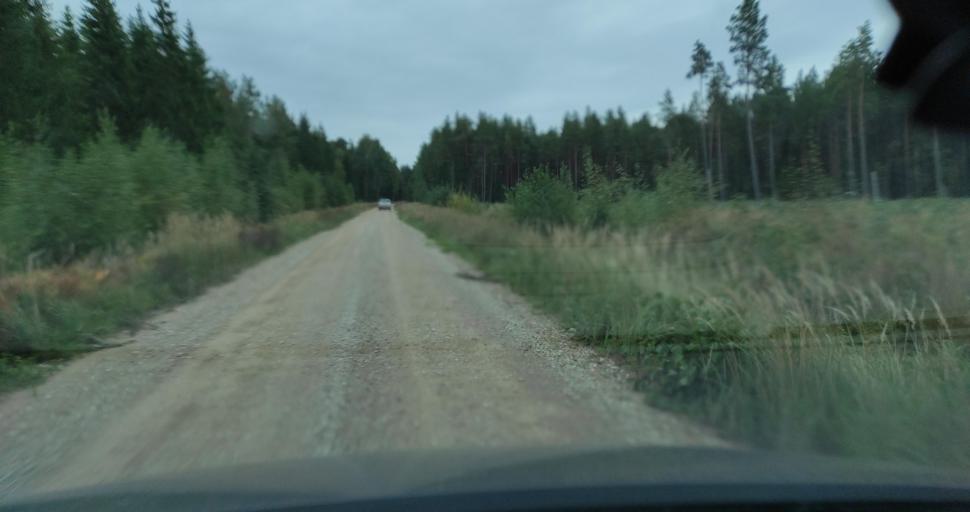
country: LV
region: Talsu Rajons
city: Stende
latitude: 57.0239
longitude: 22.3528
